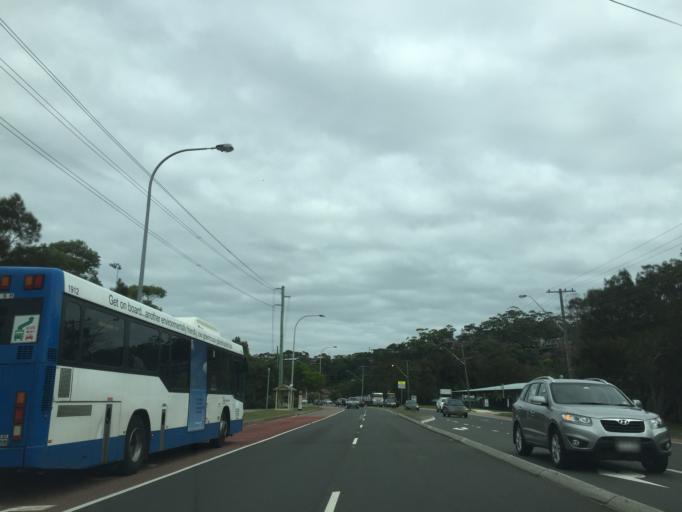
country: AU
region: New South Wales
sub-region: Pittwater
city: North Narrabeen
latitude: -33.7019
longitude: 151.2986
